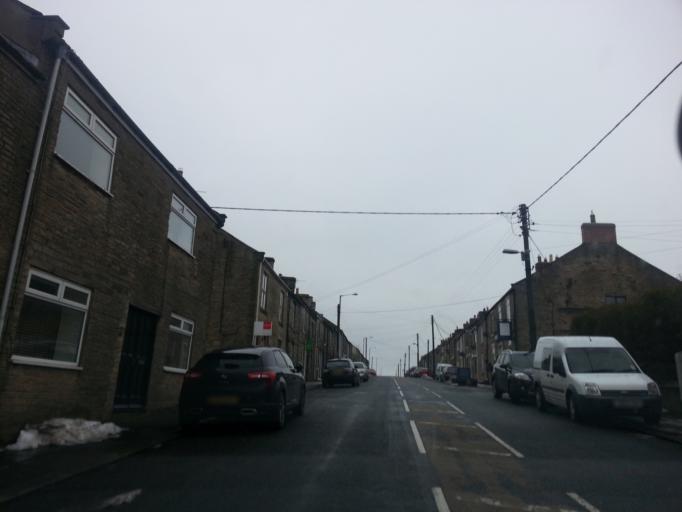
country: GB
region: England
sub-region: County Durham
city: Tow Law
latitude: 54.7405
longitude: -1.7812
